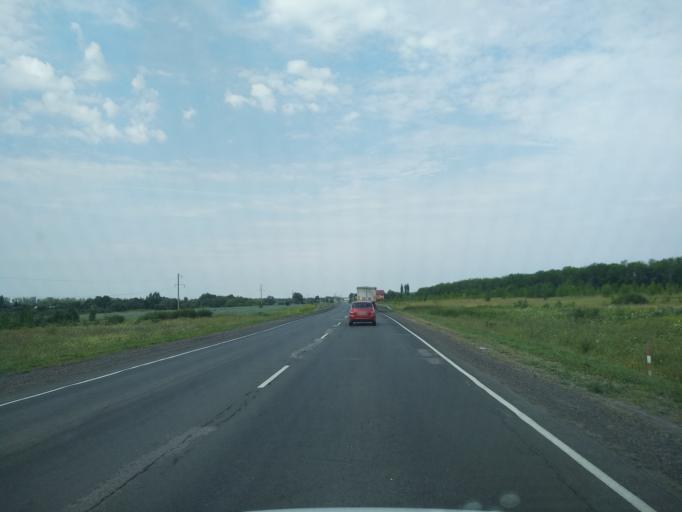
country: RU
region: Voronezj
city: Orlovo
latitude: 51.6797
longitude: 39.6583
